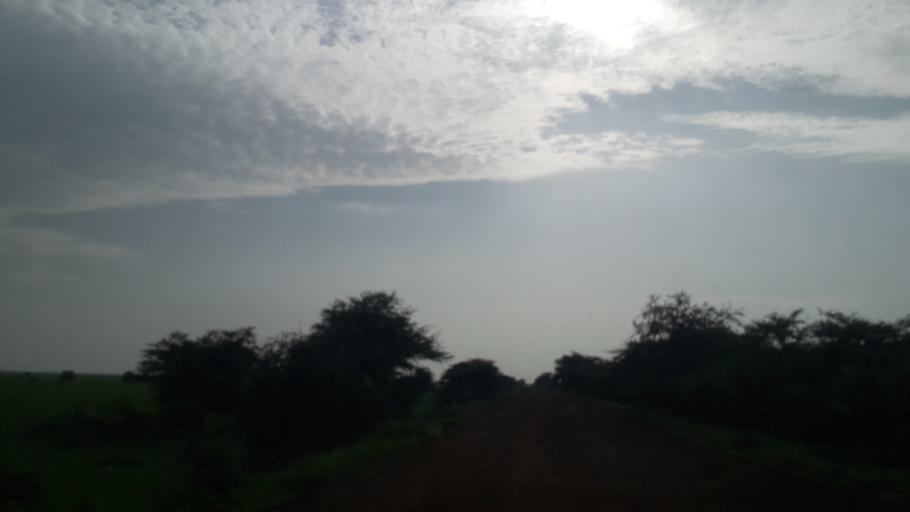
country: ET
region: Gambela
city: Gambela
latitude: 8.3502
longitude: 33.8848
